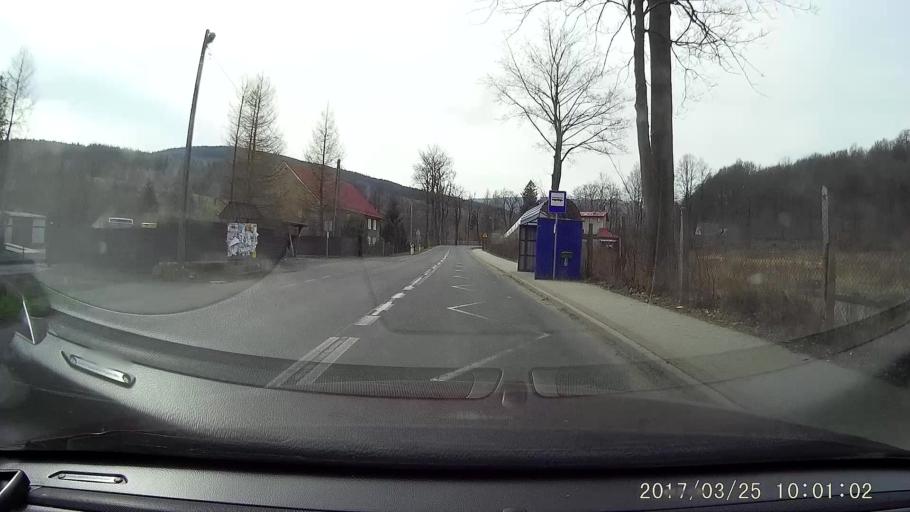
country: PL
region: Lower Silesian Voivodeship
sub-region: Powiat lubanski
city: Swieradow-Zdroj
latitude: 50.9294
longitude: 15.3542
